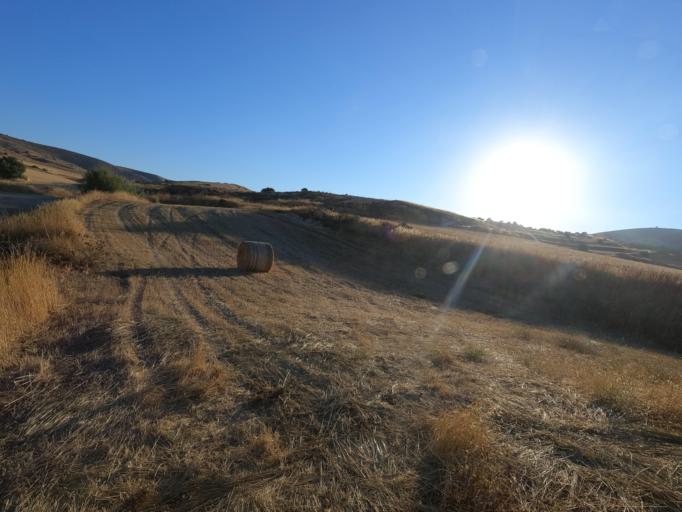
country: CY
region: Larnaka
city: Troulloi
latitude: 35.0294
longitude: 33.6476
